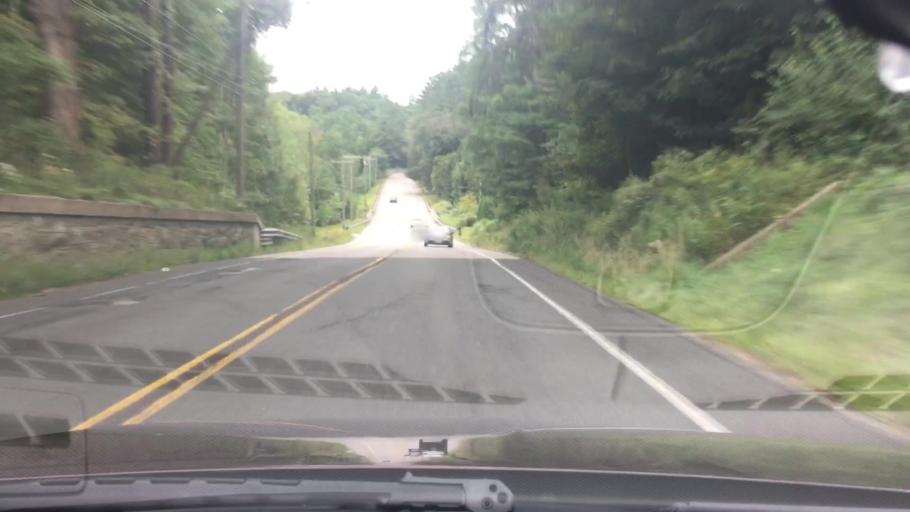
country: US
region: Connecticut
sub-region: Litchfield County
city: New Hartford Center
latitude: 41.8302
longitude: -72.9880
